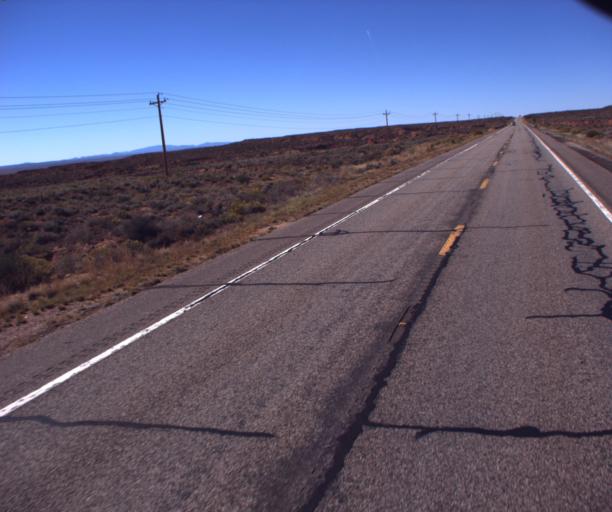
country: US
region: Arizona
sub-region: Coconino County
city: Fredonia
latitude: 36.8759
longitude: -112.6607
